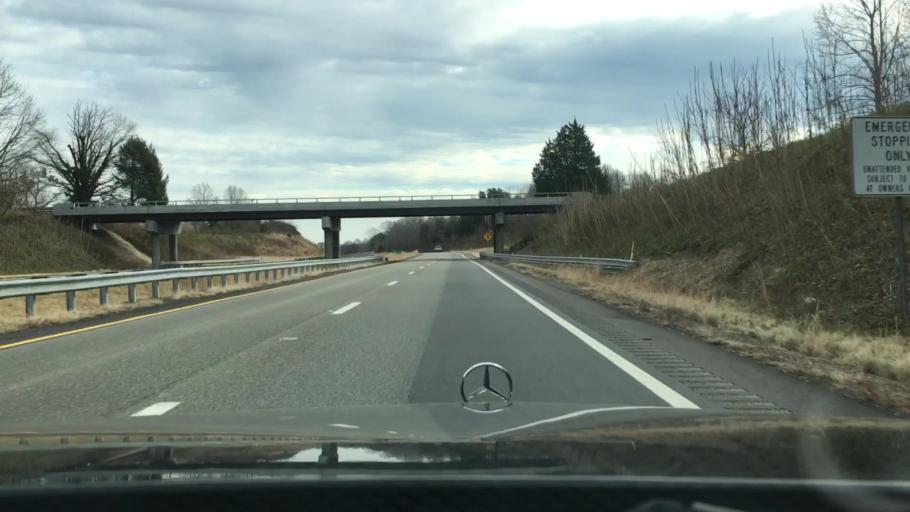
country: US
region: Virginia
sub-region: Pittsylvania County
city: Chatham
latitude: 36.8497
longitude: -79.3942
